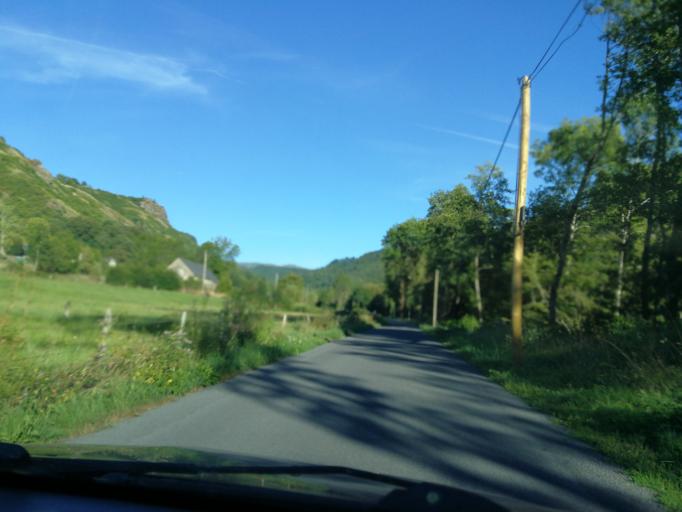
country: FR
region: Auvergne
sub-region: Departement du Cantal
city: Saint-Cernin
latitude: 45.1045
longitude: 2.5242
